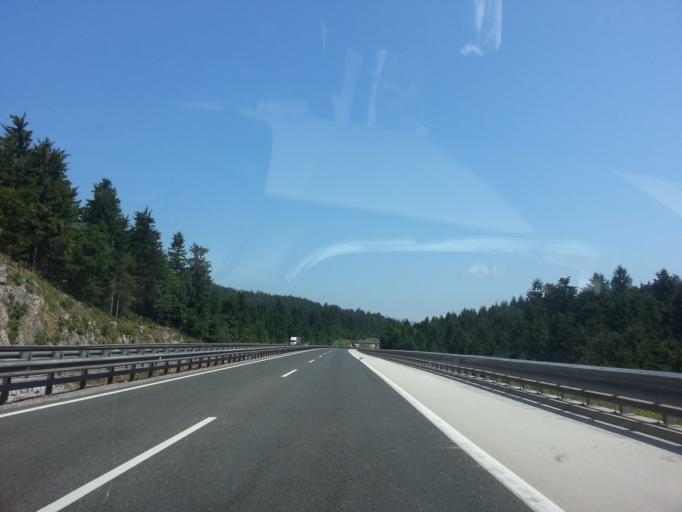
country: SI
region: Vrhnika
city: Vrhnika
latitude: 45.9288
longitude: 14.2703
